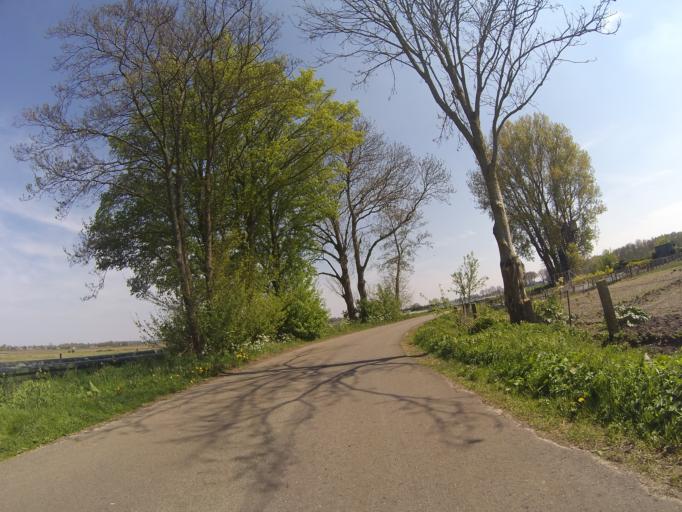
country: NL
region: Drenthe
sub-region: Gemeente Emmen
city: Schoonebeek
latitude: 52.6517
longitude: 6.8777
